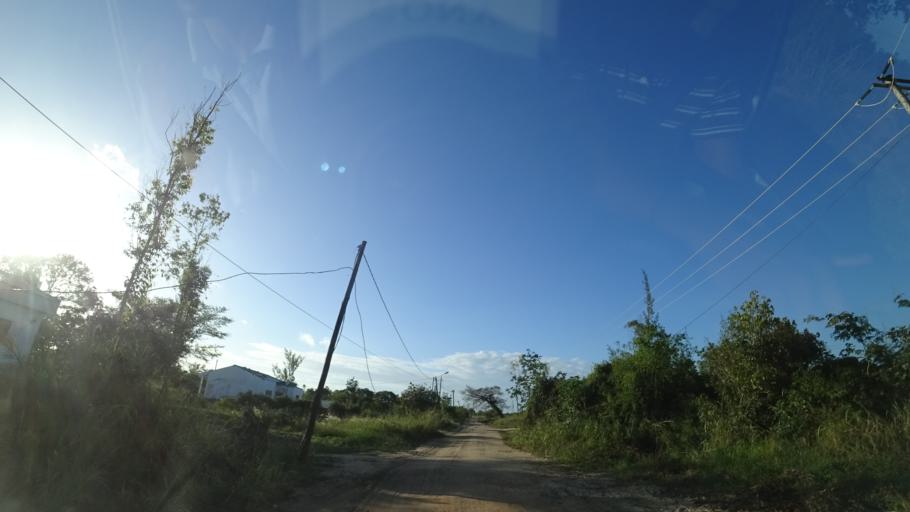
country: MZ
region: Sofala
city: Dondo
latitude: -19.3963
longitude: 34.7088
